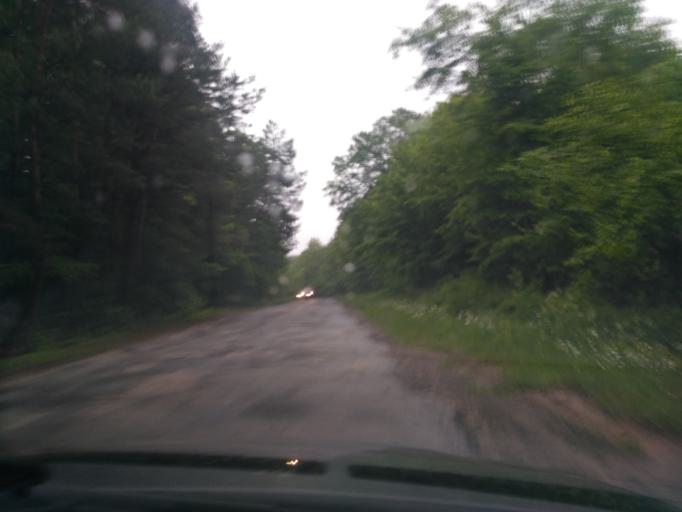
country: PL
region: Subcarpathian Voivodeship
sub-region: Powiat debicki
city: Pilzno
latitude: 49.9760
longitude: 21.3581
